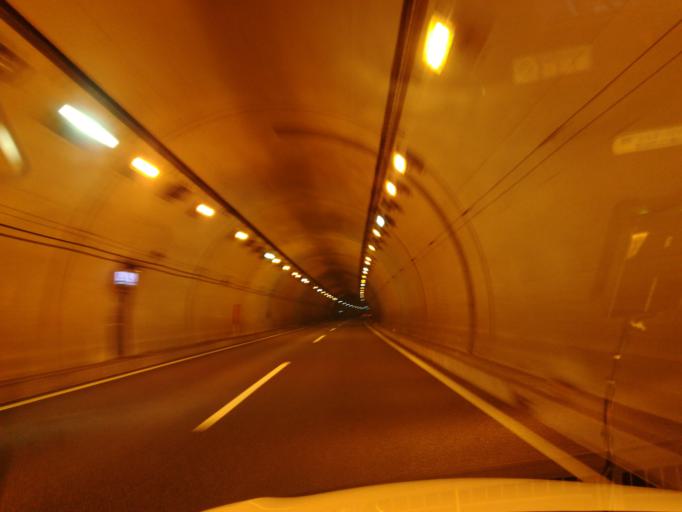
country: JP
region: Ehime
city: Kawanoecho
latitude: 33.8373
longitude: 133.6543
